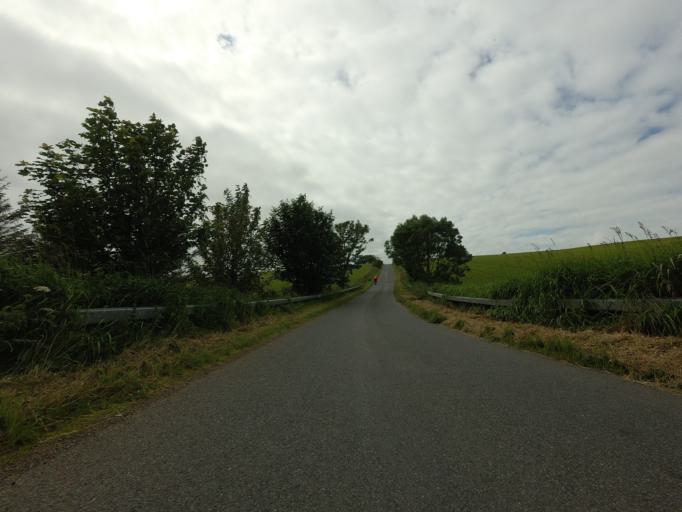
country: GB
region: Scotland
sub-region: Aberdeenshire
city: Turriff
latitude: 57.5422
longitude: -2.2690
